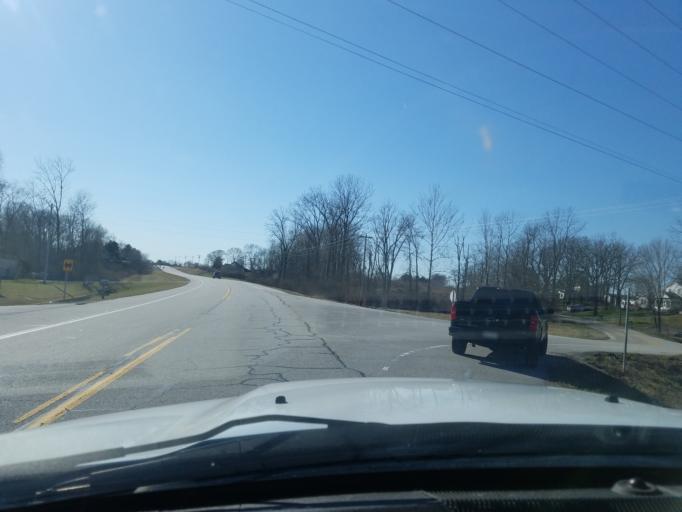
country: US
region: Indiana
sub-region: Johnson County
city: Franklin
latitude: 39.4951
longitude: -85.9646
